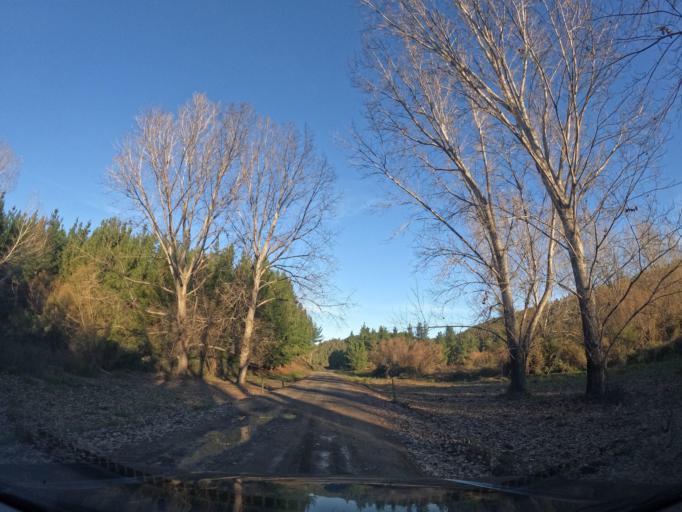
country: CL
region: Biobio
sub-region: Provincia de Concepcion
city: Chiguayante
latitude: -37.0918
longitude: -72.9015
